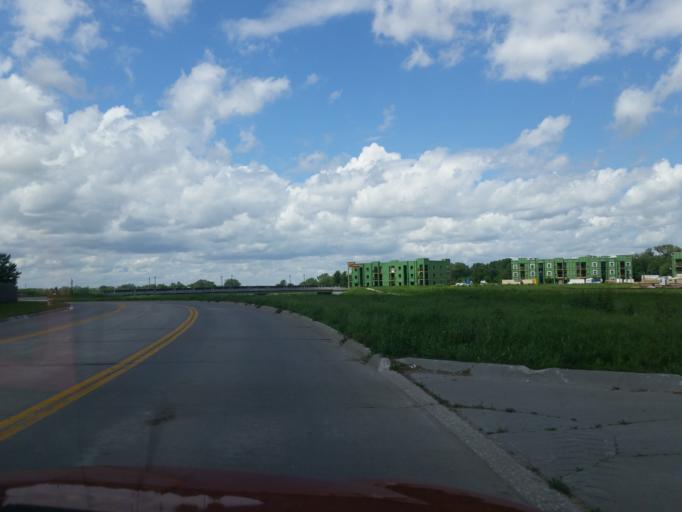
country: US
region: Nebraska
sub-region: Sarpy County
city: Offutt Air Force Base
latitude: 41.1441
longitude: -95.9765
